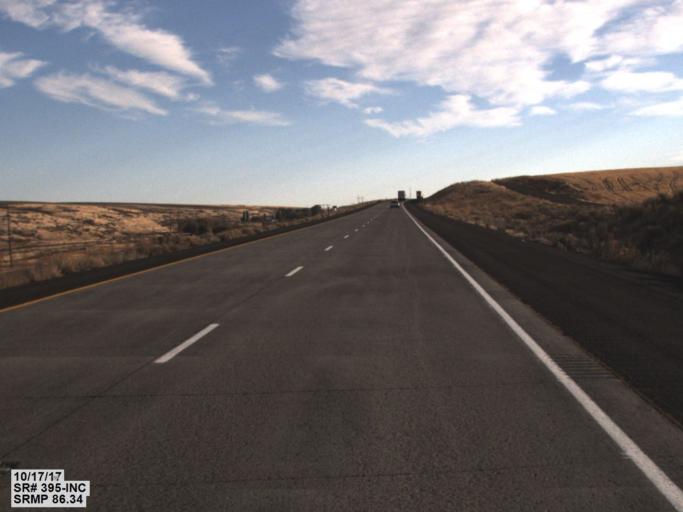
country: US
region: Washington
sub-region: Adams County
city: Ritzville
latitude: 47.0125
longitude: -118.5093
